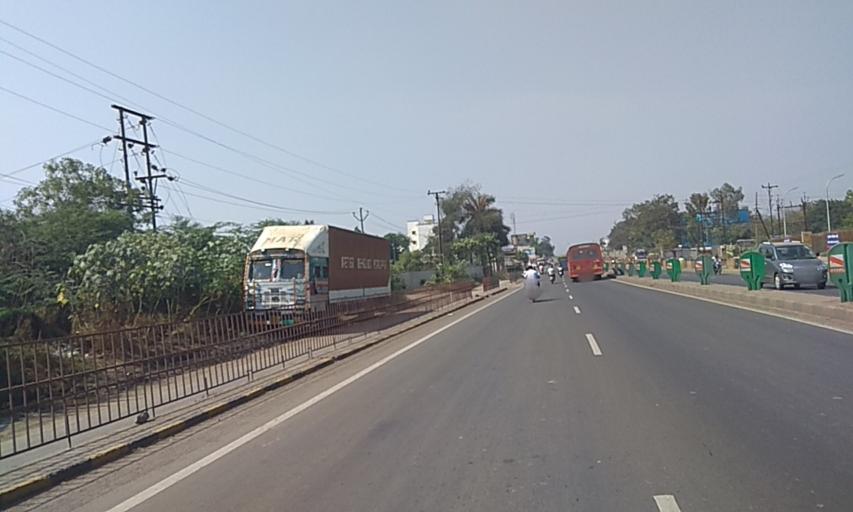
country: IN
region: Maharashtra
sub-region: Pune Division
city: Lohogaon
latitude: 18.4905
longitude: 74.0119
